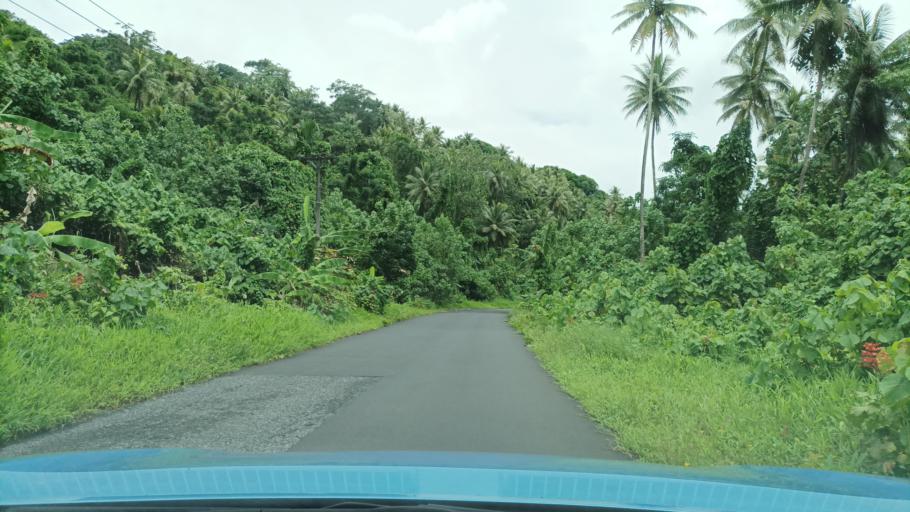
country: FM
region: Pohnpei
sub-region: Madolenihm Municipality
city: Madolenihm Municipality Government
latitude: 6.9083
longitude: 158.3222
